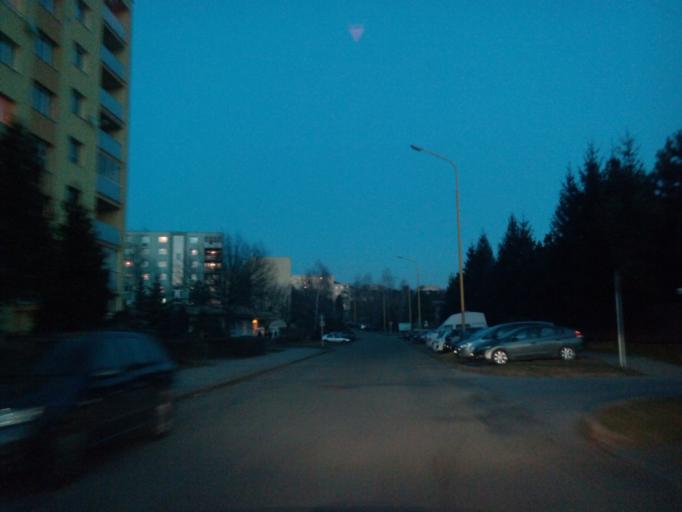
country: SK
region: Presovsky
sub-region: Okres Presov
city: Presov
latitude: 48.9841
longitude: 21.2652
